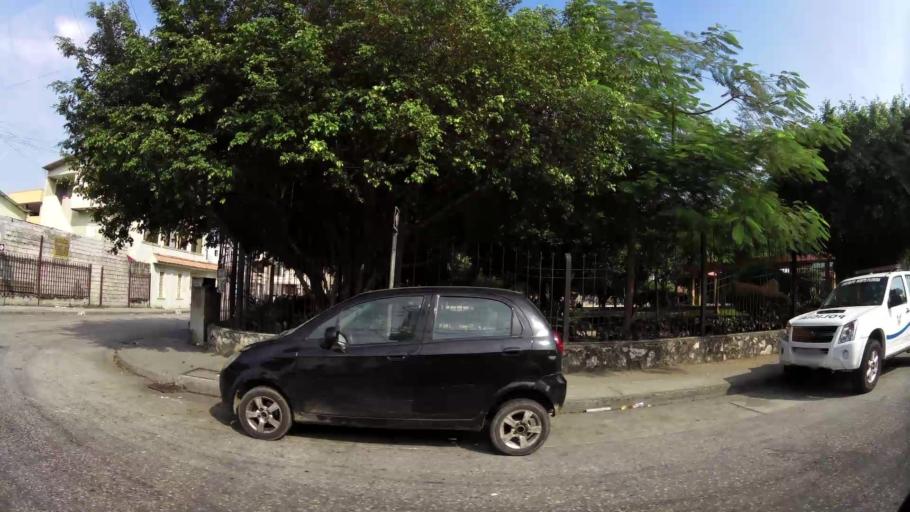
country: EC
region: Guayas
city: Guayaquil
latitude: -2.1863
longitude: -79.9102
